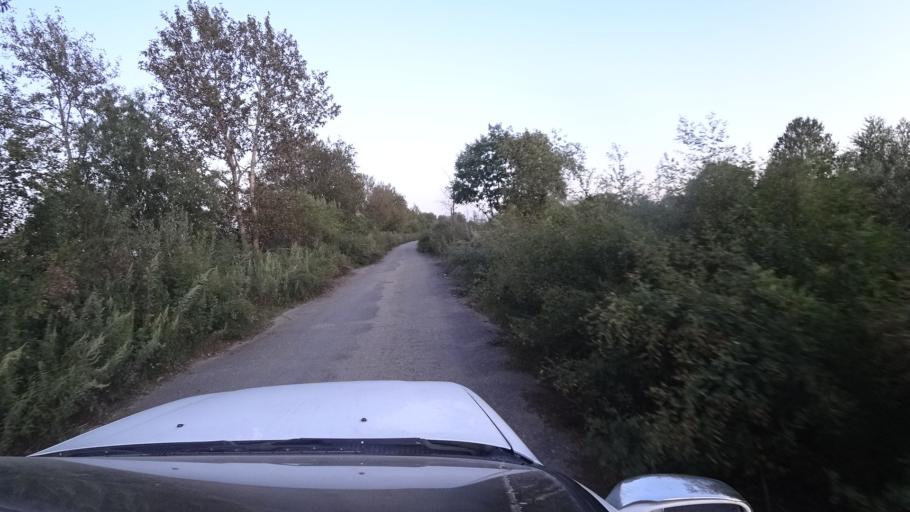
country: RU
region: Primorskiy
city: Dal'nerechensk
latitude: 45.9474
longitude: 133.7632
